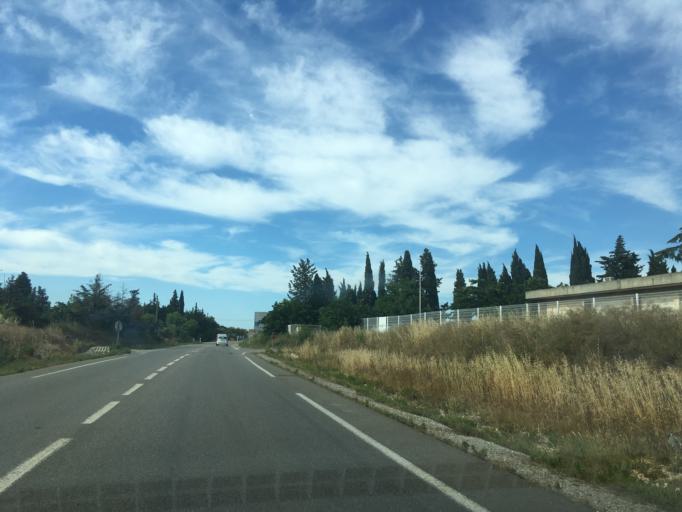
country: FR
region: Languedoc-Roussillon
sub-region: Departement du Gard
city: Bouillargues
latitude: 43.7886
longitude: 4.4292
